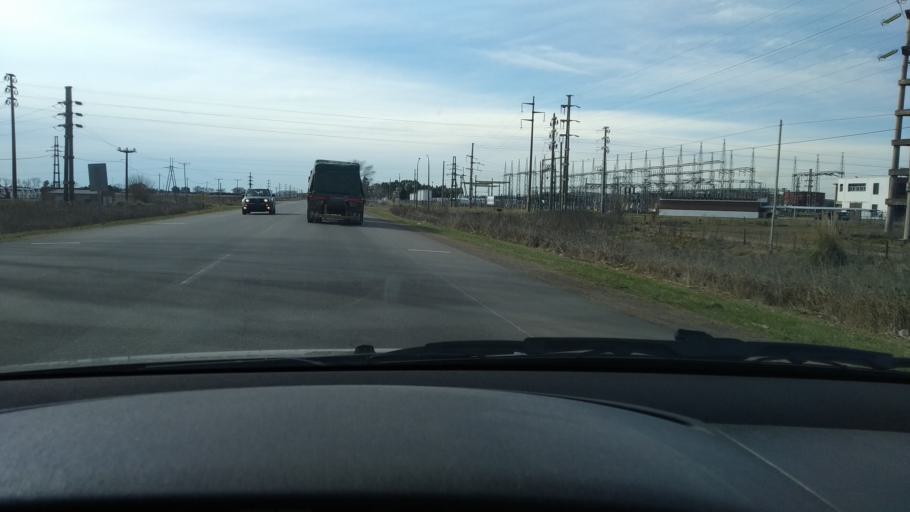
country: AR
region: Buenos Aires
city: Olavarria
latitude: -36.9452
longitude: -60.2408
